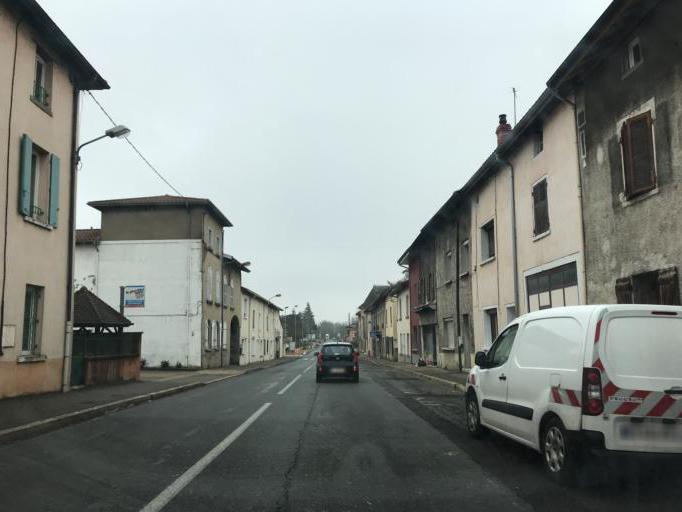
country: FR
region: Rhone-Alpes
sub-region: Departement de l'Ain
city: Villars-les-Dombes
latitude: 45.9996
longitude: 5.0296
